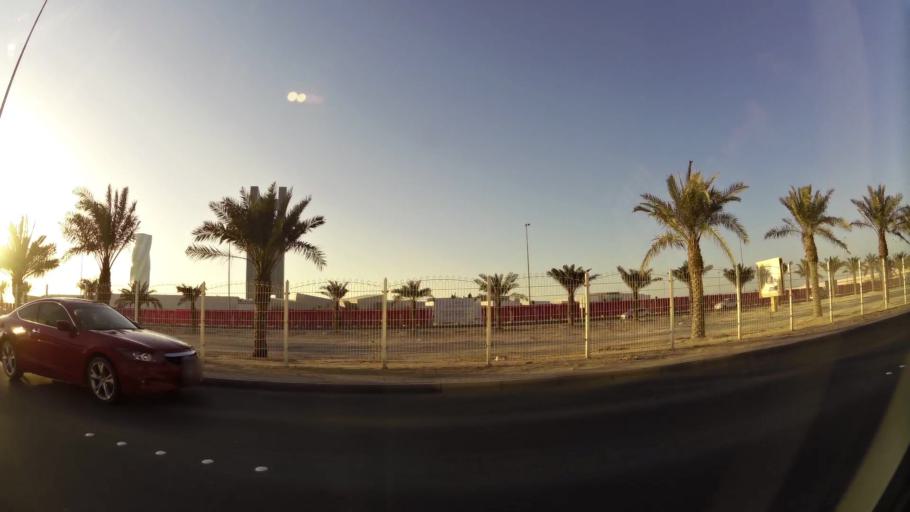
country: BH
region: Muharraq
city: Al Muharraq
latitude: 26.2440
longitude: 50.5873
